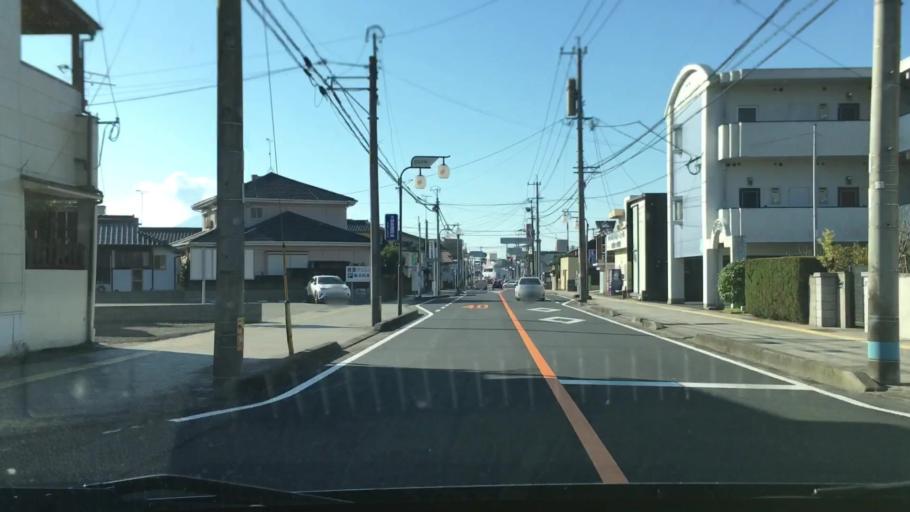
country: JP
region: Kagoshima
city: Kajiki
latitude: 31.7425
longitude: 130.6686
